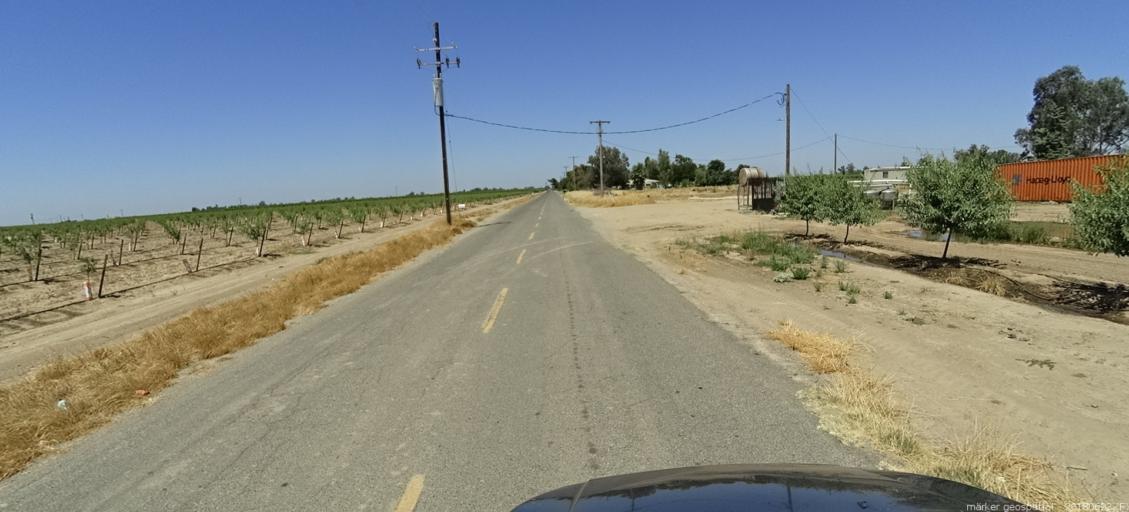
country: US
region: California
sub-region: Madera County
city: Chowchilla
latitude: 37.0983
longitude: -120.2343
